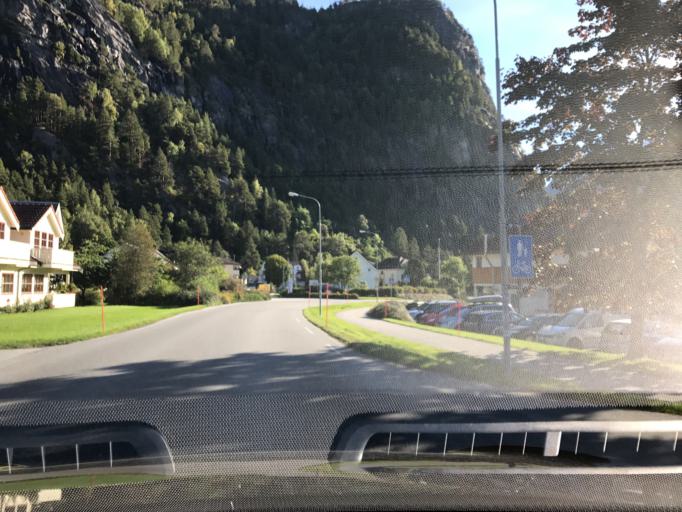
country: NO
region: More og Romsdal
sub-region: Norddal
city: Valldal
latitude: 62.3007
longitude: 7.2602
